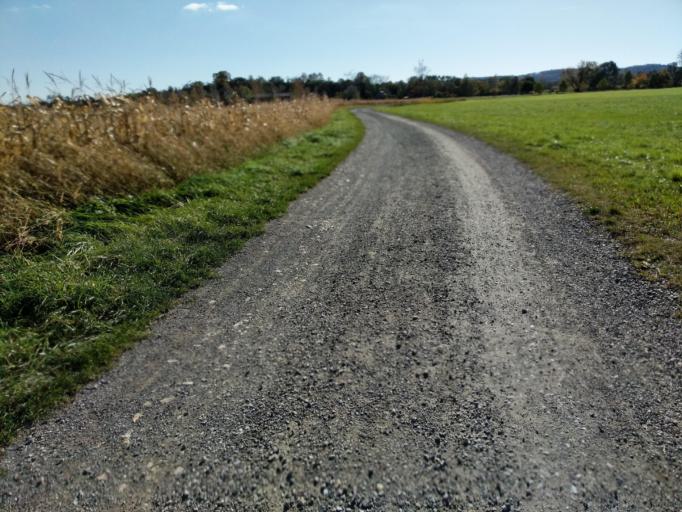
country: DE
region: Baden-Wuerttemberg
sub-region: Tuebingen Region
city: Salem
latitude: 47.7513
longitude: 9.2985
